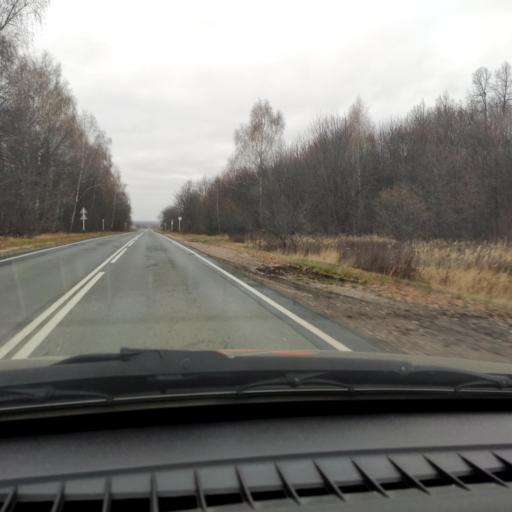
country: RU
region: Samara
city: Zhigulevsk
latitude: 53.3398
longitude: 49.4898
